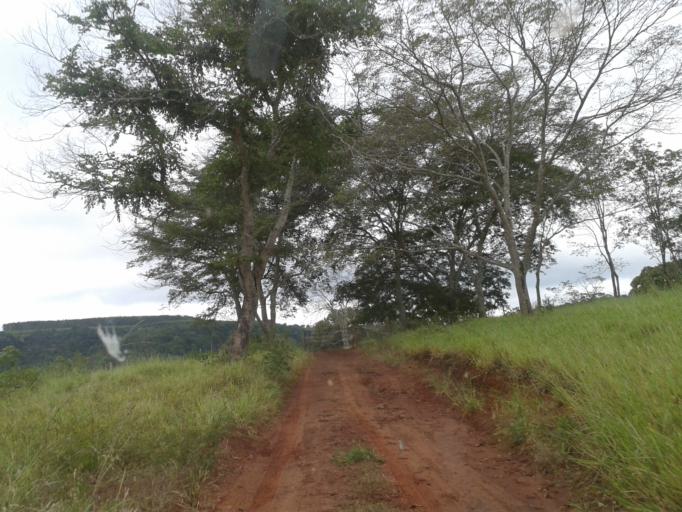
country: BR
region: Minas Gerais
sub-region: Campina Verde
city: Campina Verde
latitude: -19.4666
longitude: -49.5886
